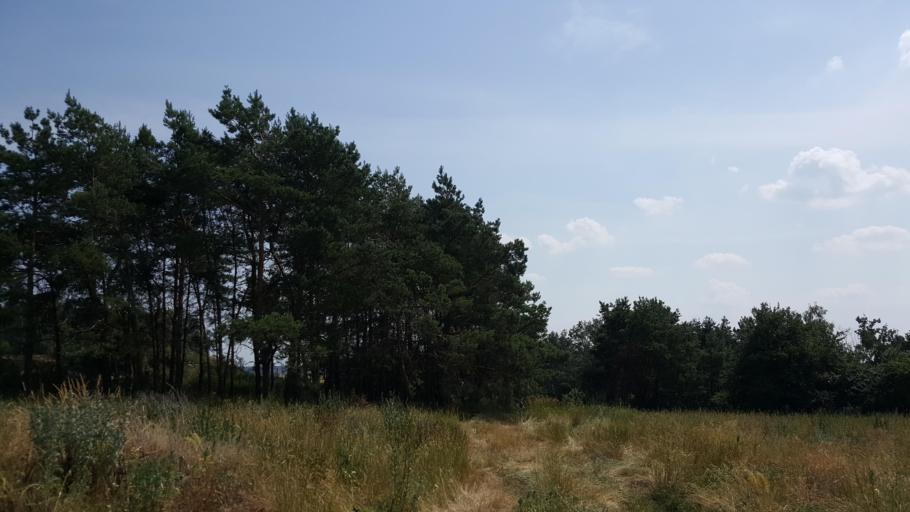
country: BY
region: Brest
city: Kamyanyets
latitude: 52.3440
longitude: 23.7679
